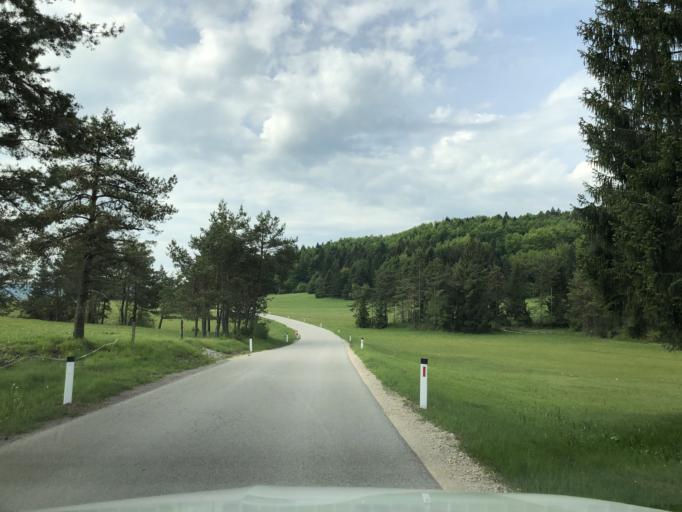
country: SI
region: Bloke
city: Nova Vas
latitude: 45.7873
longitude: 14.4993
